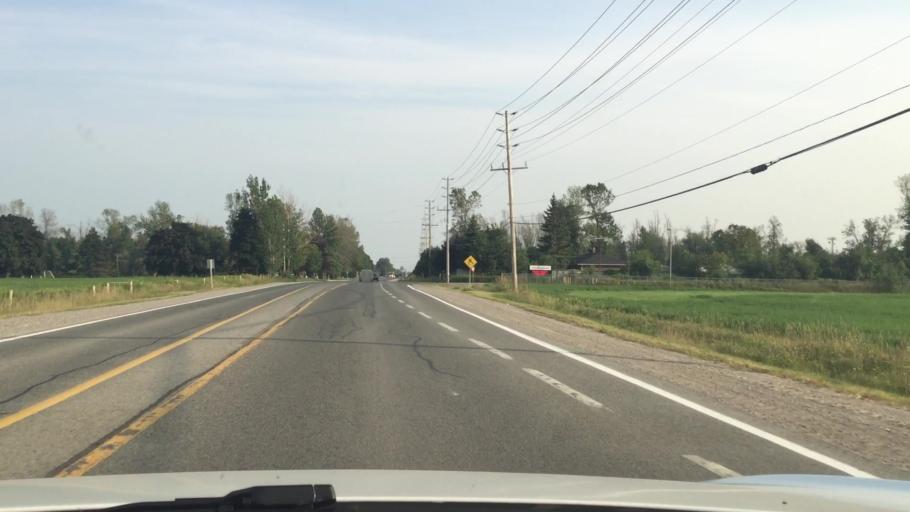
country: CA
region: Ontario
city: Oshawa
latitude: 43.9035
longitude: -78.7742
